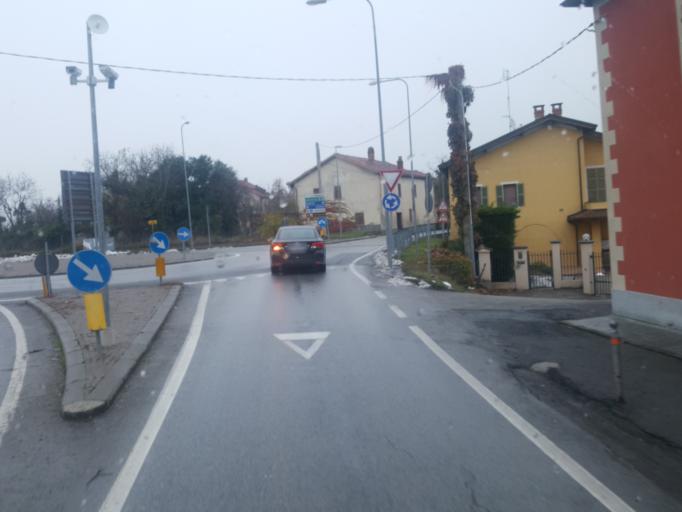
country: IT
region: Piedmont
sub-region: Provincia di Cuneo
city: Breo
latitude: 44.4052
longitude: 7.8314
